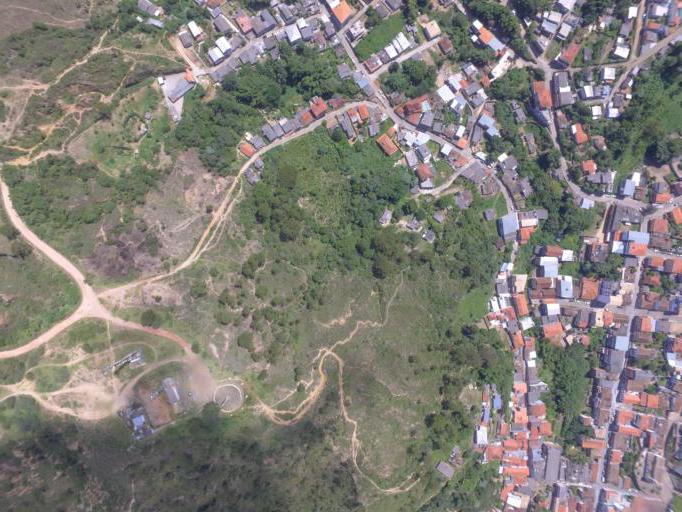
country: BR
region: Minas Gerais
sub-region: Tiradentes
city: Tiradentes
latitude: -21.0542
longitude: -44.0777
